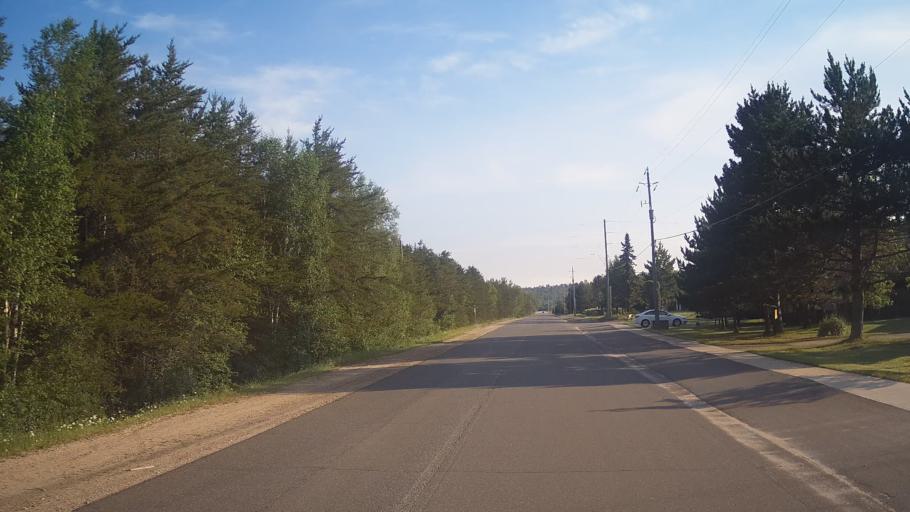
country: CA
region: Ontario
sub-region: Rainy River District
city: Atikokan
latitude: 49.4092
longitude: -91.6663
